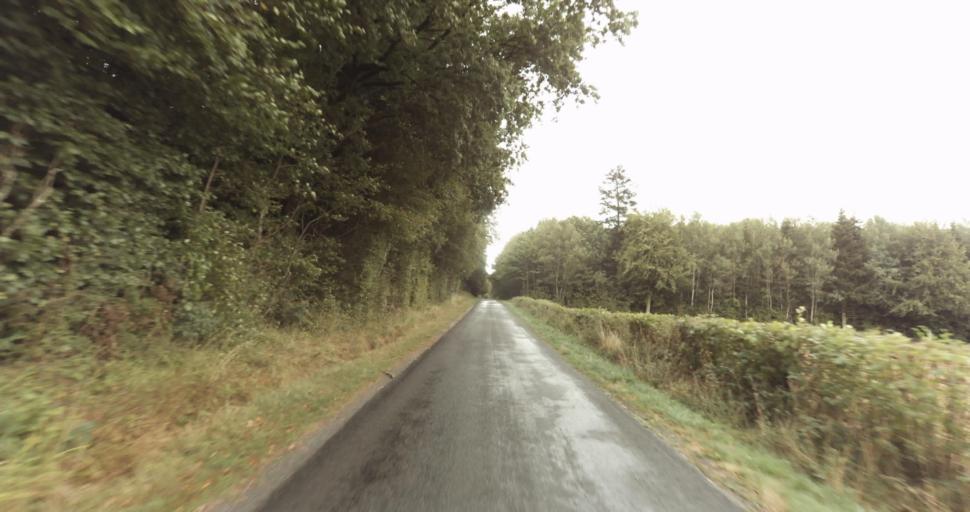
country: FR
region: Lower Normandy
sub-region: Departement de l'Orne
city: Sainte-Gauburge-Sainte-Colombe
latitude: 48.7460
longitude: 0.4838
